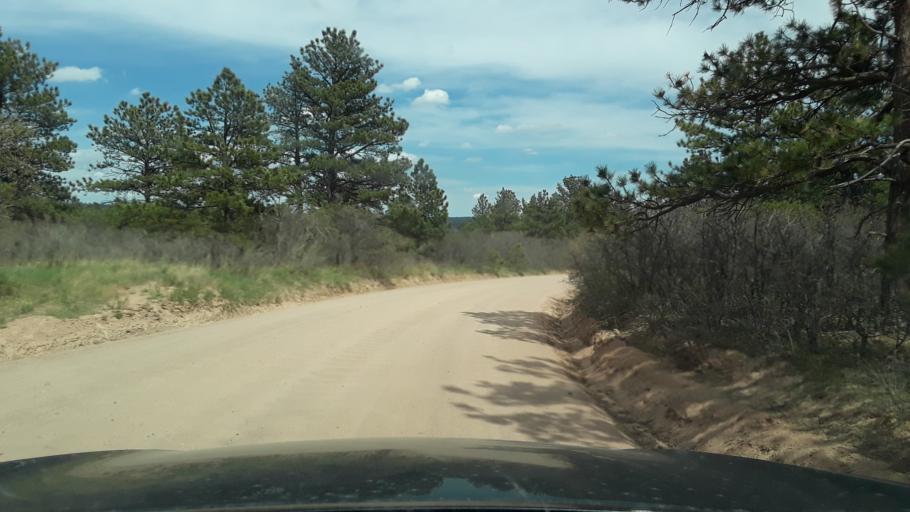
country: US
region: Colorado
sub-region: El Paso County
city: Monument
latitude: 39.0904
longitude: -104.9023
